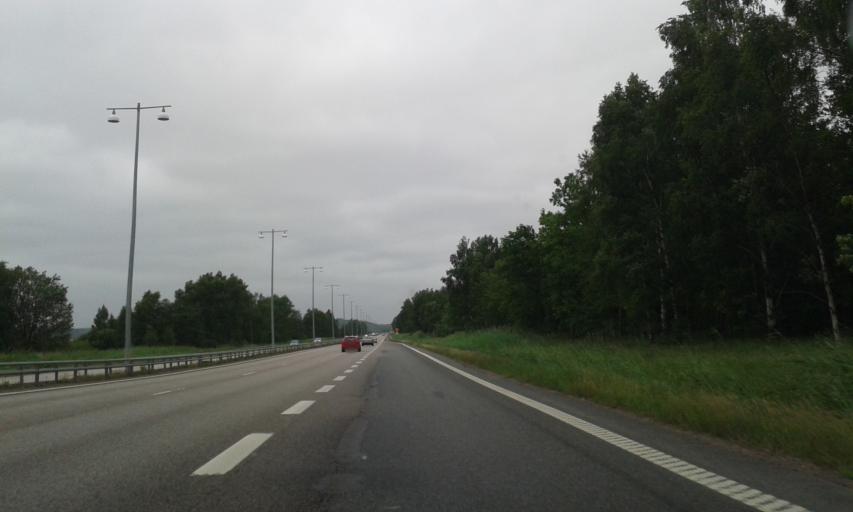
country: SE
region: Vaestra Goetaland
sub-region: Goteborg
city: Hammarkullen
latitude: 57.7687
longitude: 12.0092
